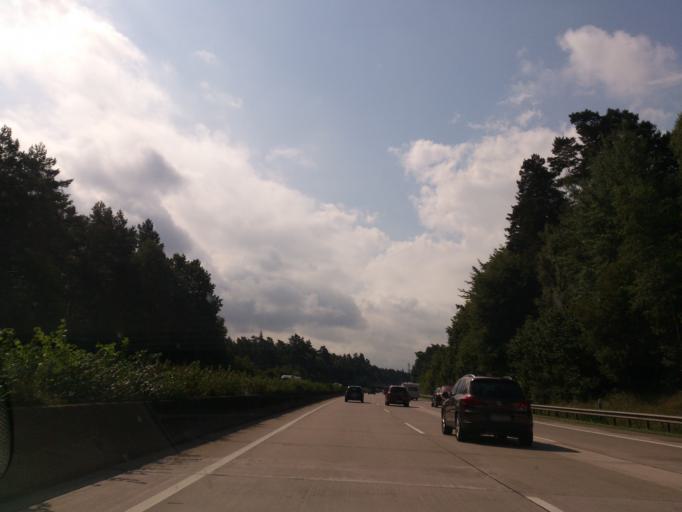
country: DE
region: Lower Saxony
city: Toppenstedt
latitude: 53.2627
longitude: 10.0875
